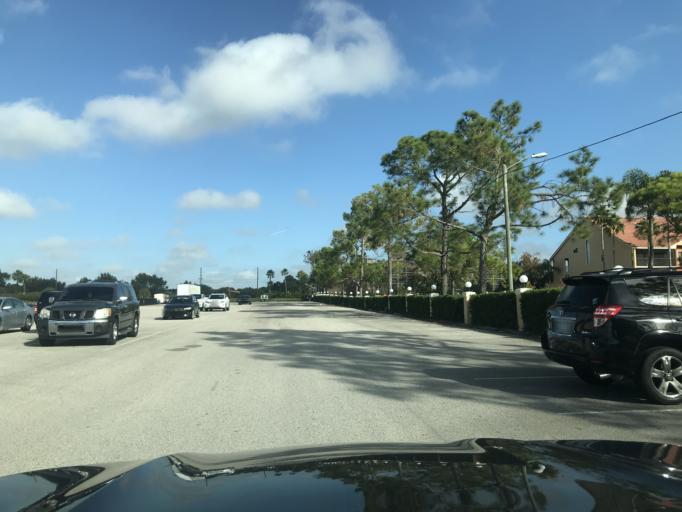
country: US
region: Florida
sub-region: Polk County
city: Citrus Ridge
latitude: 28.3305
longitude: -81.5929
